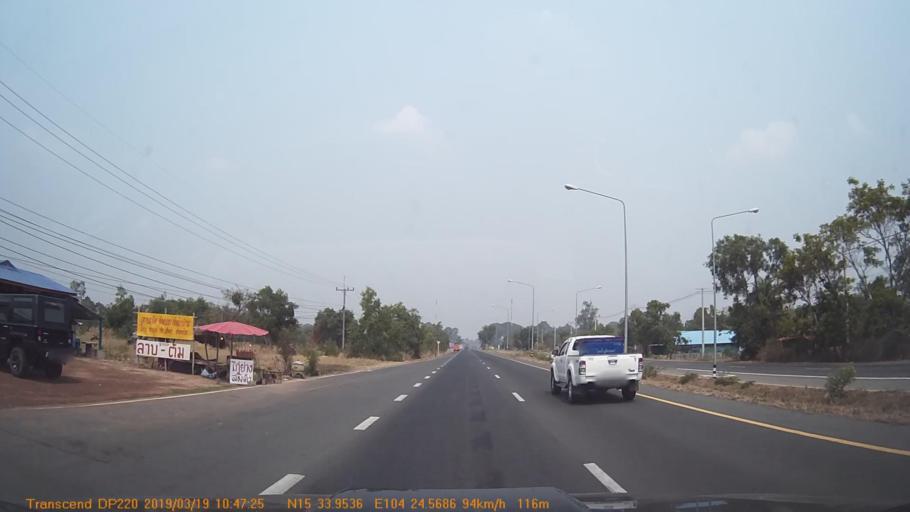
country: TH
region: Yasothon
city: Kham Khuean Kaeo
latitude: 15.5663
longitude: 104.4092
